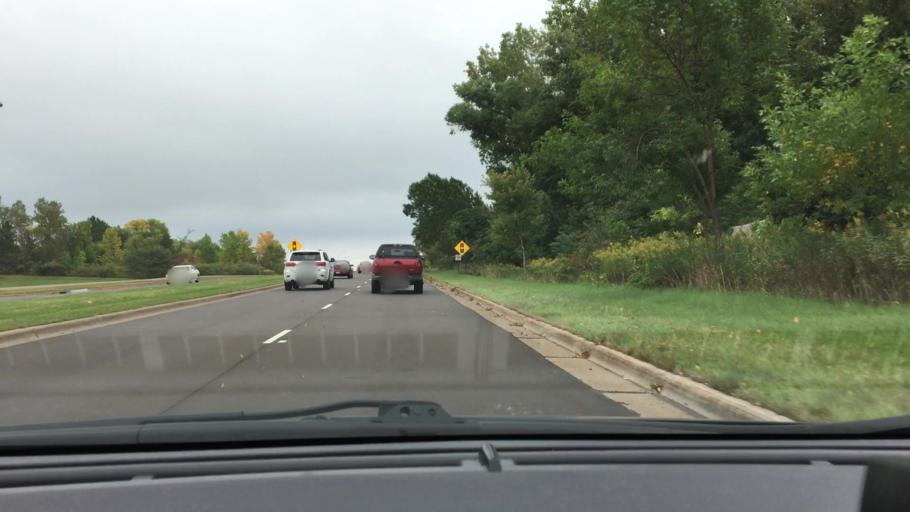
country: US
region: Minnesota
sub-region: Hennepin County
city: Plymouth
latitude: 45.0334
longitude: -93.4253
